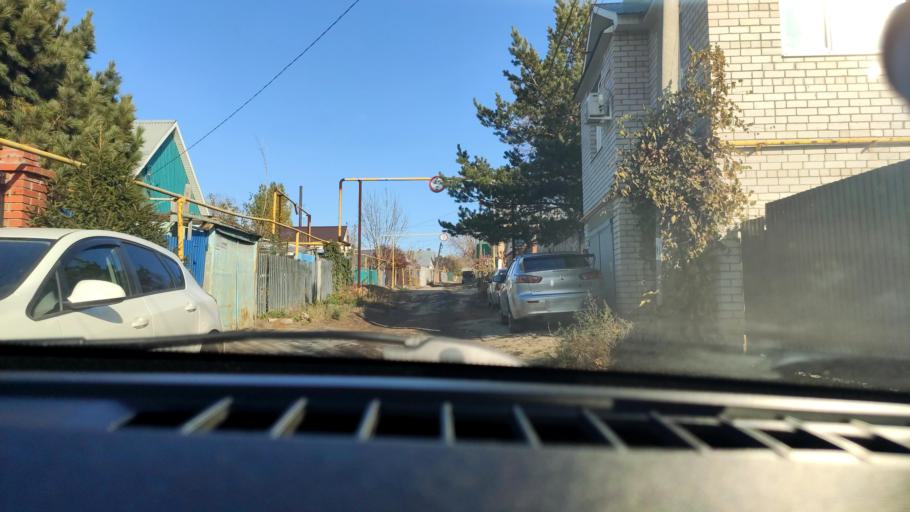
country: RU
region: Samara
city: Samara
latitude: 53.1802
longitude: 50.1533
